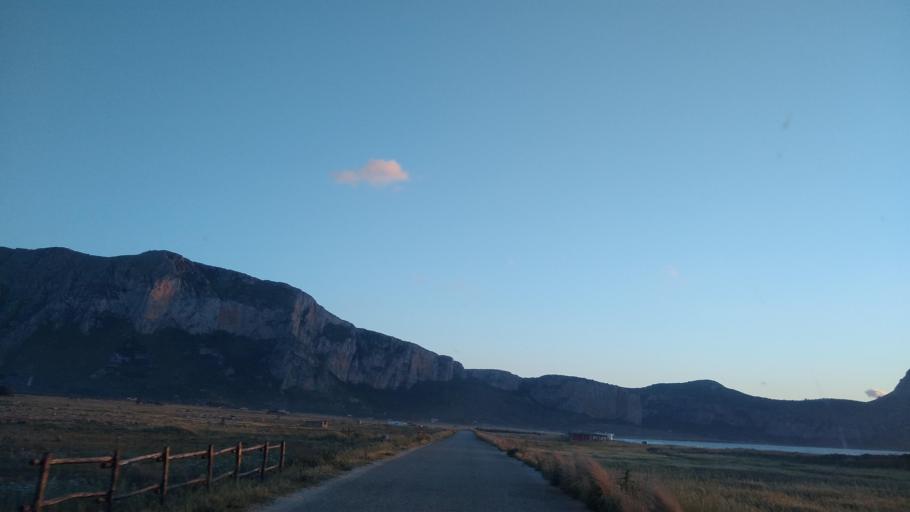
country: IT
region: Sicily
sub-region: Trapani
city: Castelluzzo
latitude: 38.1214
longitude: 12.7246
